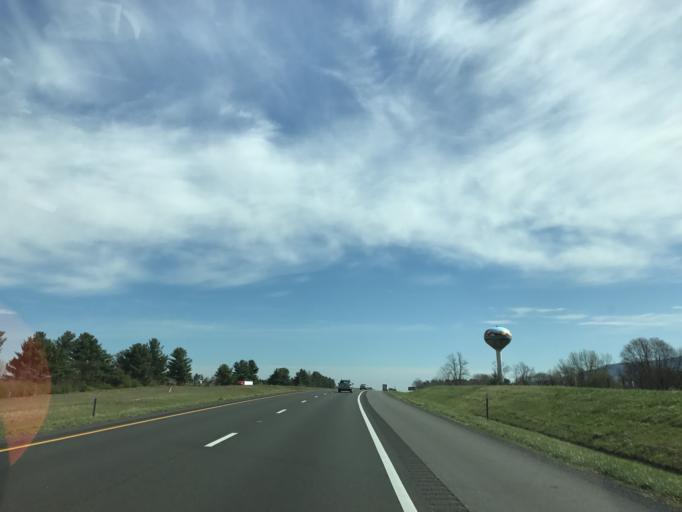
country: US
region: Virginia
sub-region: Shenandoah County
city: Mount Jackson
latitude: 38.7519
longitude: -78.6467
